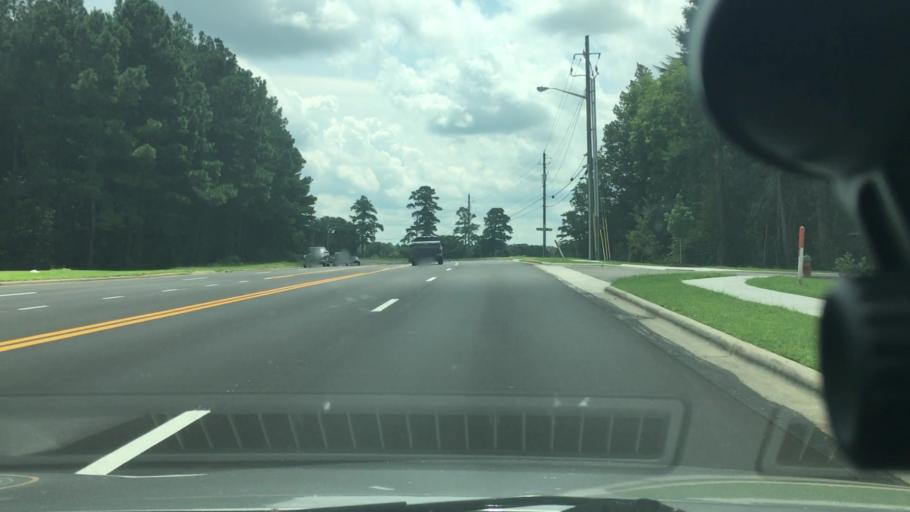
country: US
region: North Carolina
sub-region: Pitt County
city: Greenville
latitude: 35.5880
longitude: -77.3163
